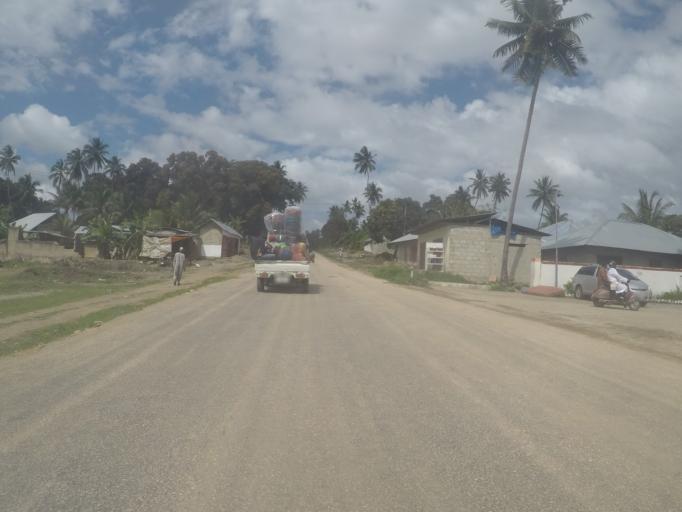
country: TZ
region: Zanzibar North
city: Mkokotoni
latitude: -5.8753
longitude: 39.2604
